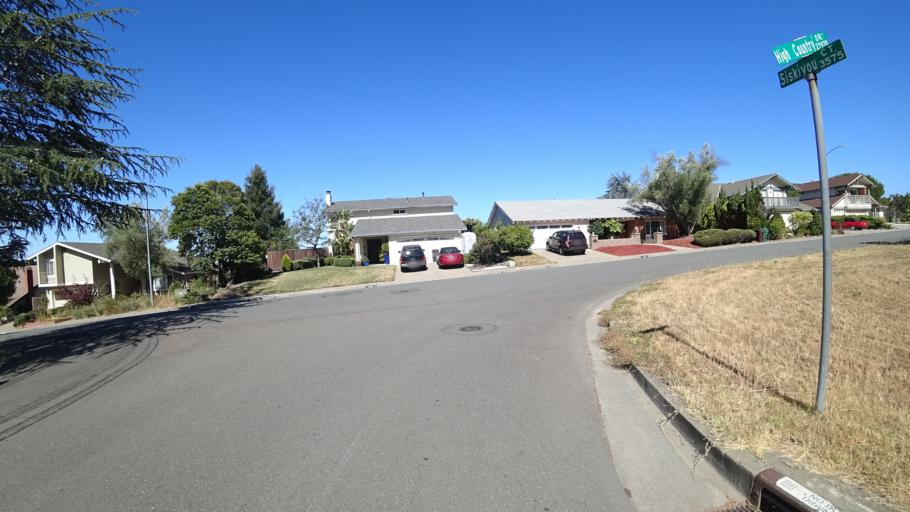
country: US
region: California
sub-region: Alameda County
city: Fairview
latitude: 37.6523
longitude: -122.0284
